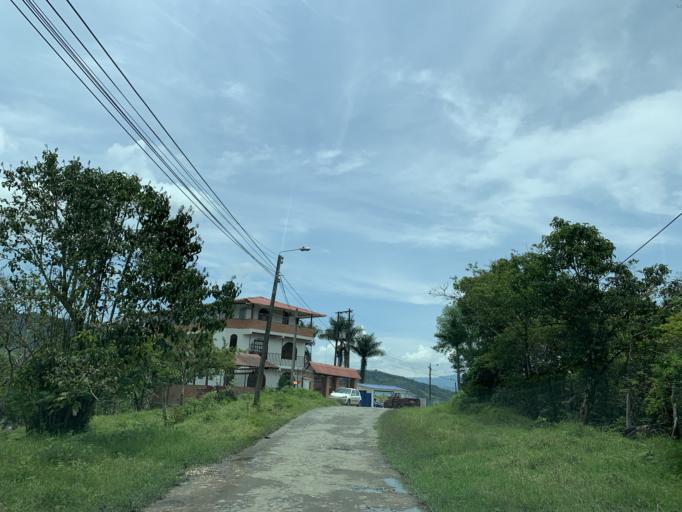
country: CO
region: Boyaca
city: Moniquira
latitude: 5.8733
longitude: -73.5650
